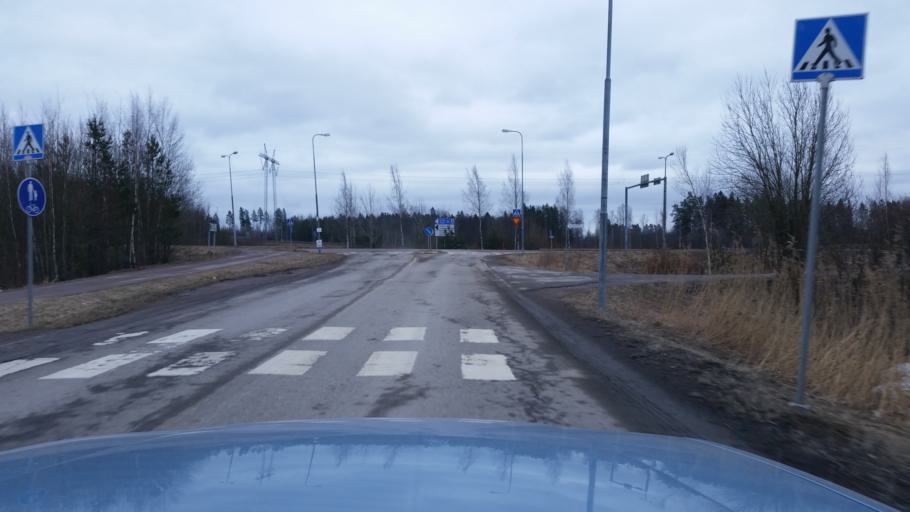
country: FI
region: Uusimaa
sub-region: Helsinki
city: Kauniainen
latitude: 60.2527
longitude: 24.7082
